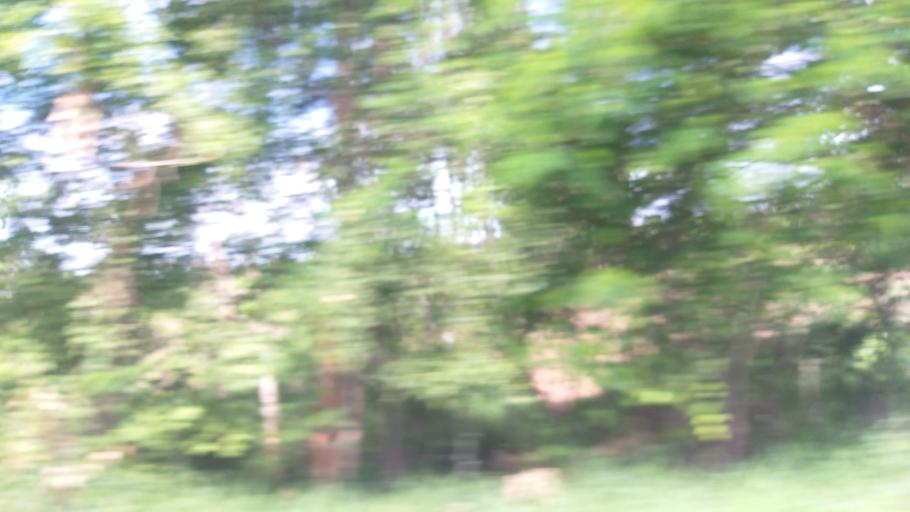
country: TH
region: Khon Kaen
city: Nong Ruea
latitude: 16.4740
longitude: 102.4411
